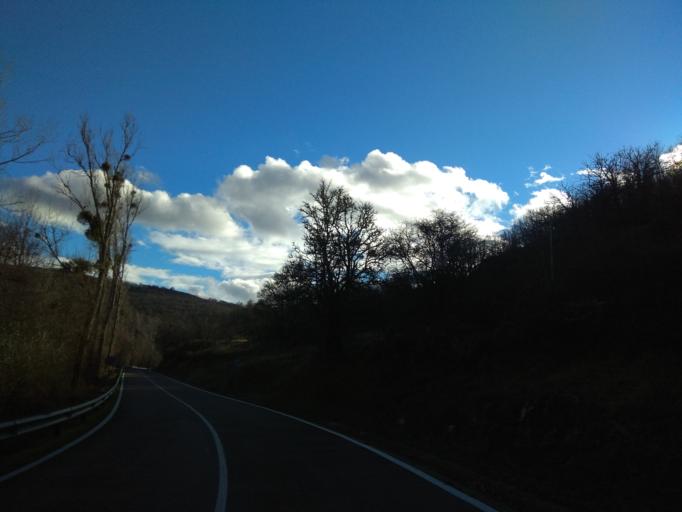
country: ES
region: Cantabria
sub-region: Provincia de Cantabria
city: San Martin de Elines
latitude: 42.8839
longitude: -3.9114
